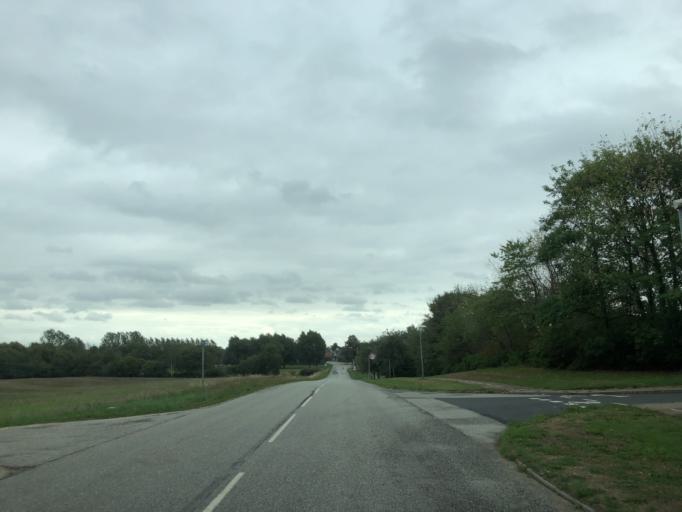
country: DK
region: Central Jutland
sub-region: Herning Kommune
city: Snejbjerg
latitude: 56.1740
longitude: 8.8429
